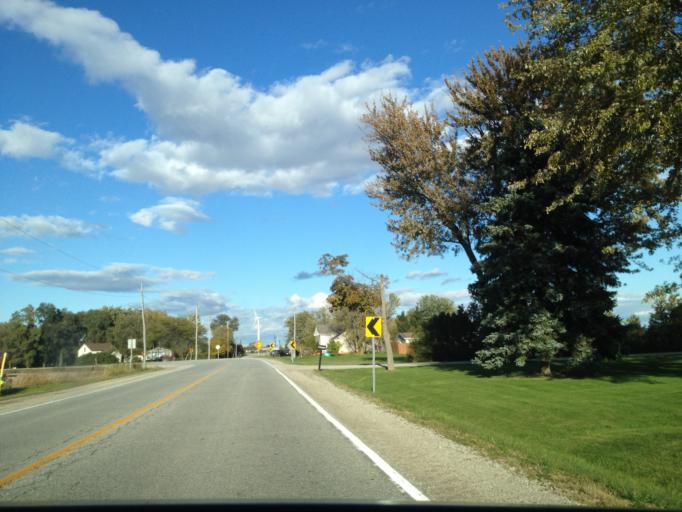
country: US
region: Michigan
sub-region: Wayne County
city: Grosse Pointe
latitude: 42.1348
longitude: -82.7348
